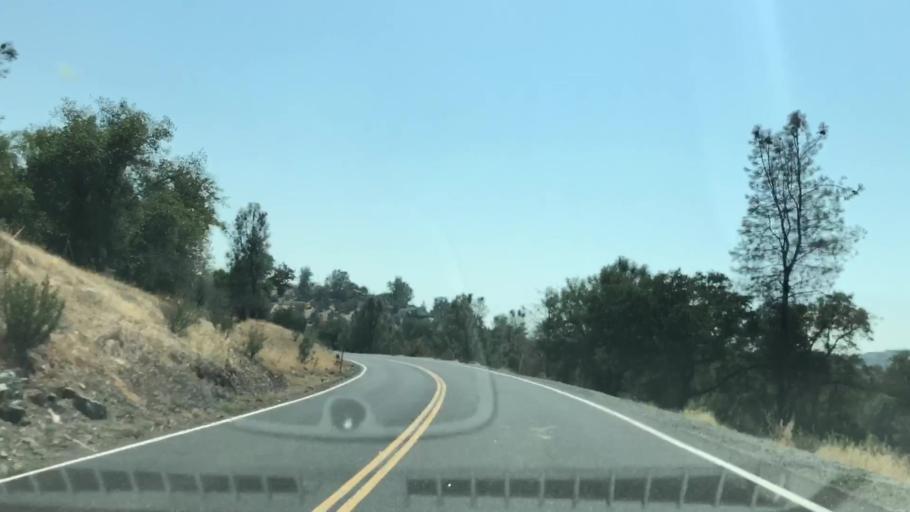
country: US
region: California
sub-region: Calaveras County
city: Copperopolis
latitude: 37.9532
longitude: -120.6142
